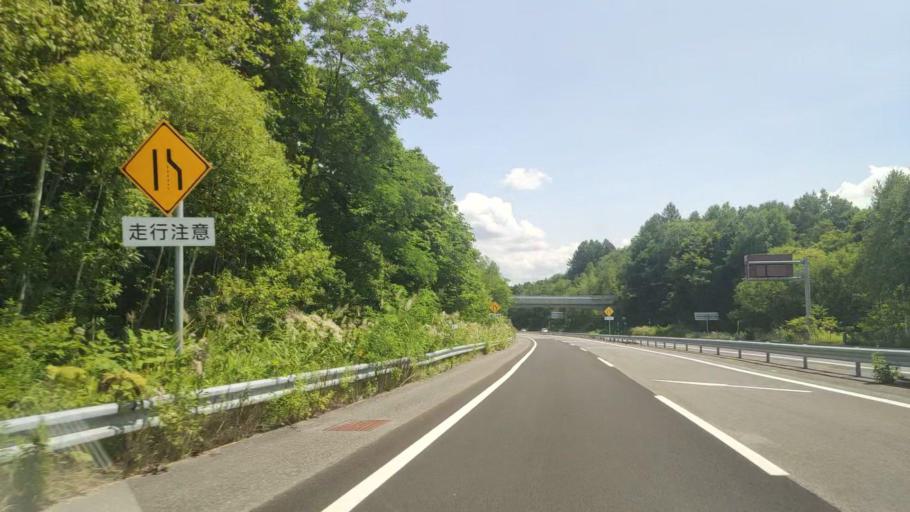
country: JP
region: Hokkaido
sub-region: Asahikawa-shi
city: Asahikawa
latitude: 43.9160
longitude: 142.5033
